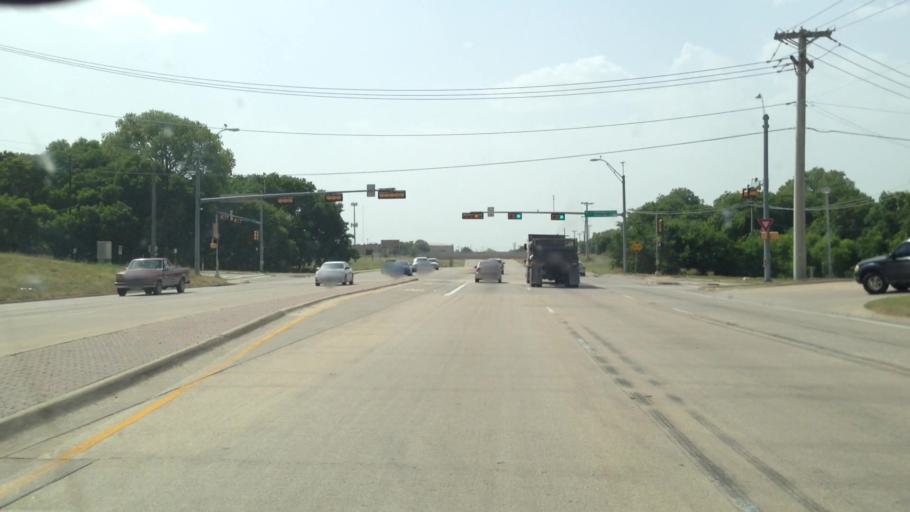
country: US
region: Texas
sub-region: Collin County
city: McKinney
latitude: 33.2072
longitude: -96.6052
